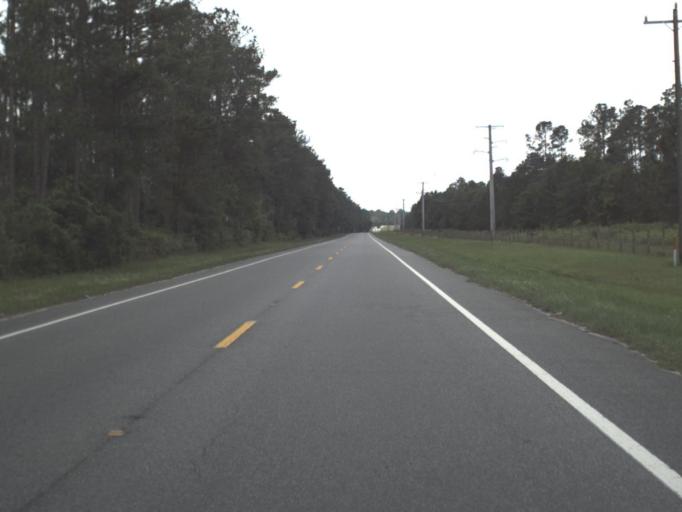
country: US
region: Florida
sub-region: Clay County
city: Asbury Lake
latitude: 29.9199
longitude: -81.8973
